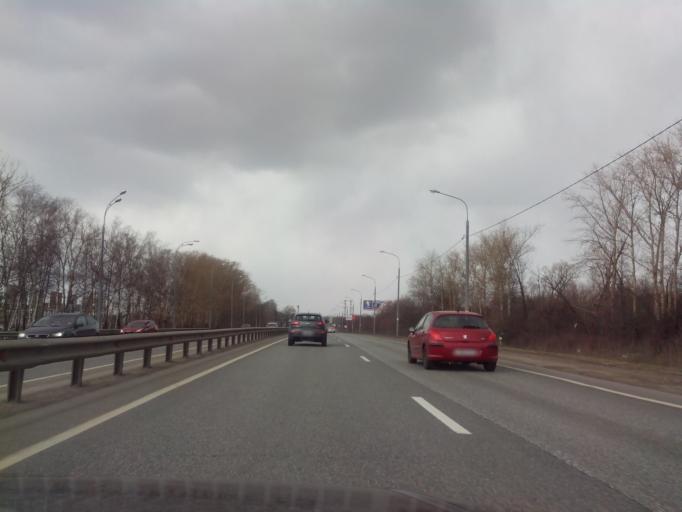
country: RU
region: Moskovskaya
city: Noginsk
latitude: 55.8330
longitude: 38.3959
